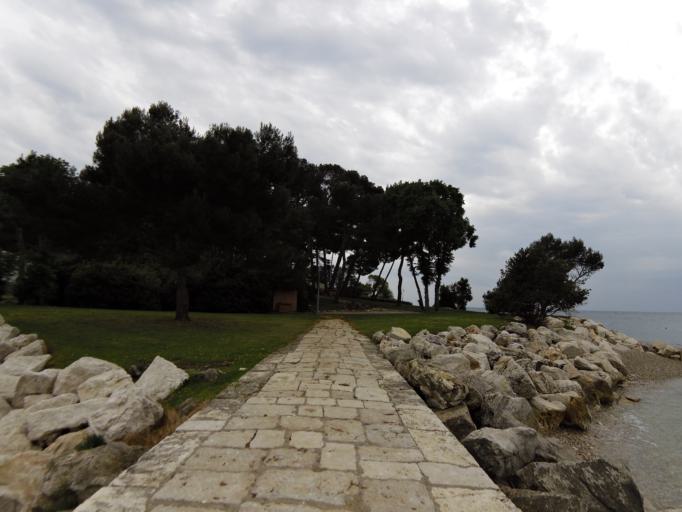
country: HR
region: Istarska
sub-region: Grad Porec
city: Porec
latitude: 45.2267
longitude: 13.5837
